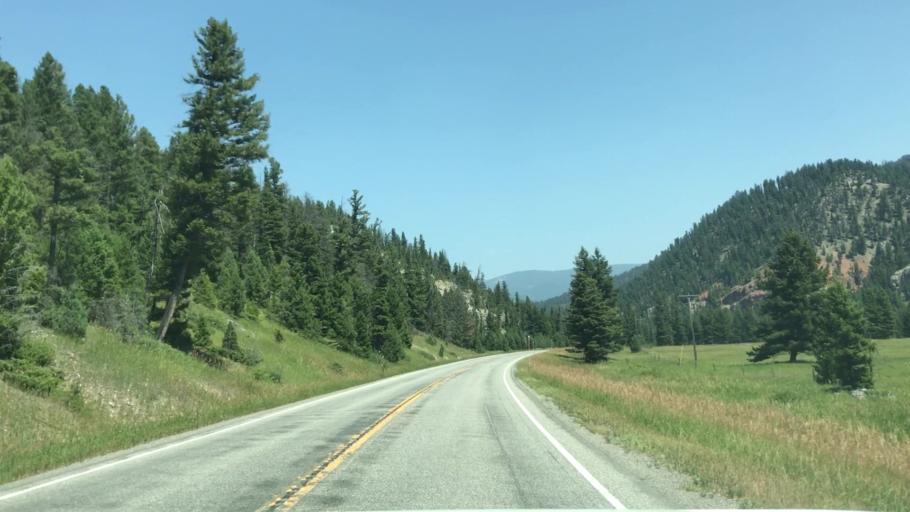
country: US
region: Montana
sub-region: Gallatin County
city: Big Sky
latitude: 45.1643
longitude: -111.2480
